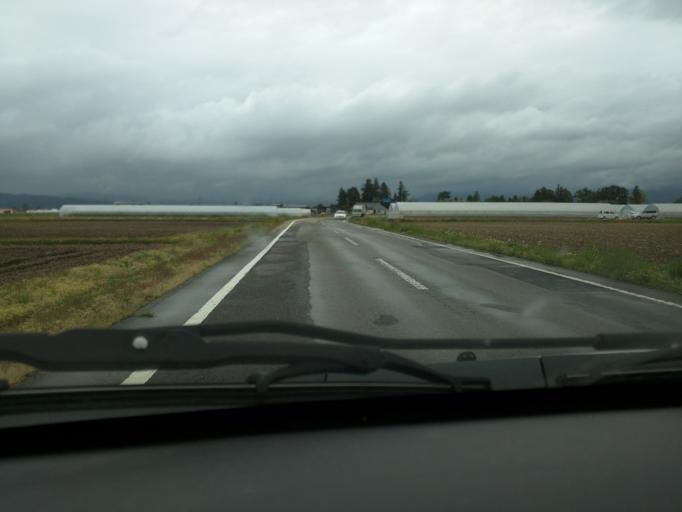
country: JP
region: Fukushima
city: Kitakata
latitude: 37.6042
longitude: 139.8731
